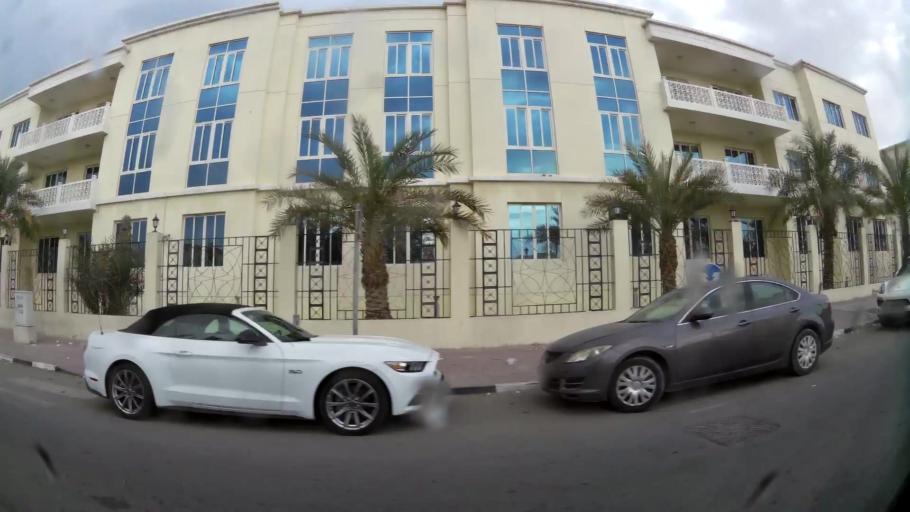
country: QA
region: Baladiyat ad Dawhah
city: Doha
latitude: 25.2719
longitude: 51.4995
